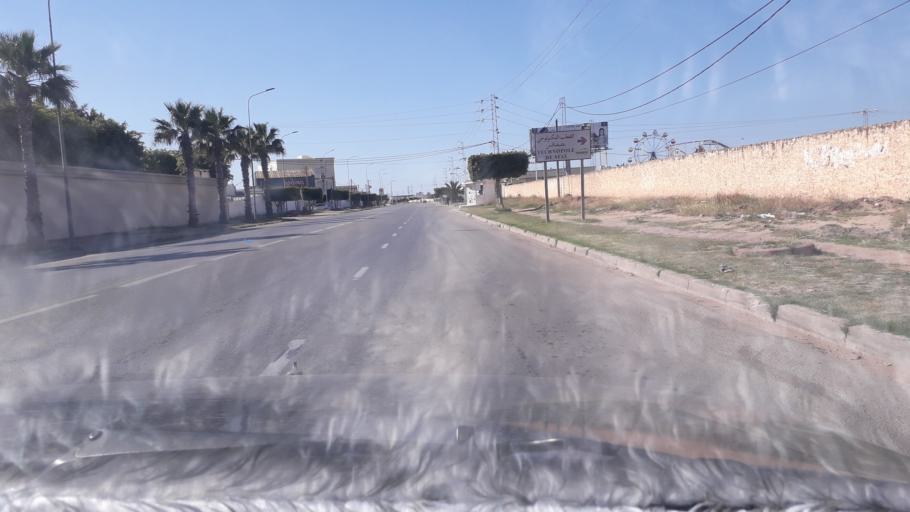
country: TN
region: Safaqis
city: Al Qarmadah
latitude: 34.8467
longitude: 10.7621
